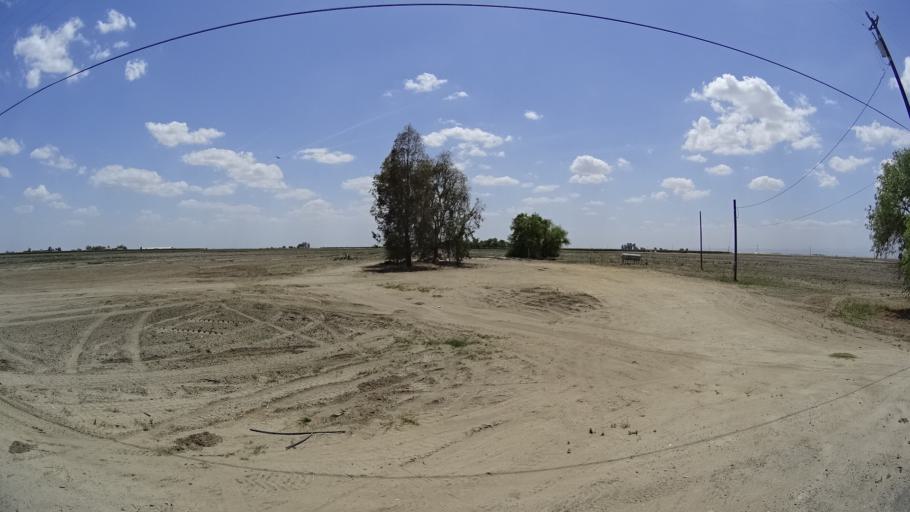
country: US
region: California
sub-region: Kings County
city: Stratford
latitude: 36.1821
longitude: -119.8122
